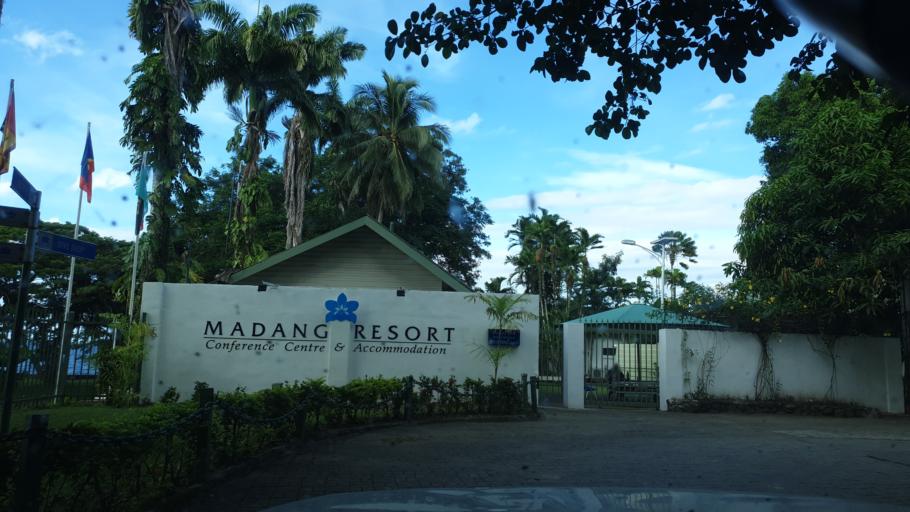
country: PG
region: Madang
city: Madang
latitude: -5.2081
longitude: 145.8094
